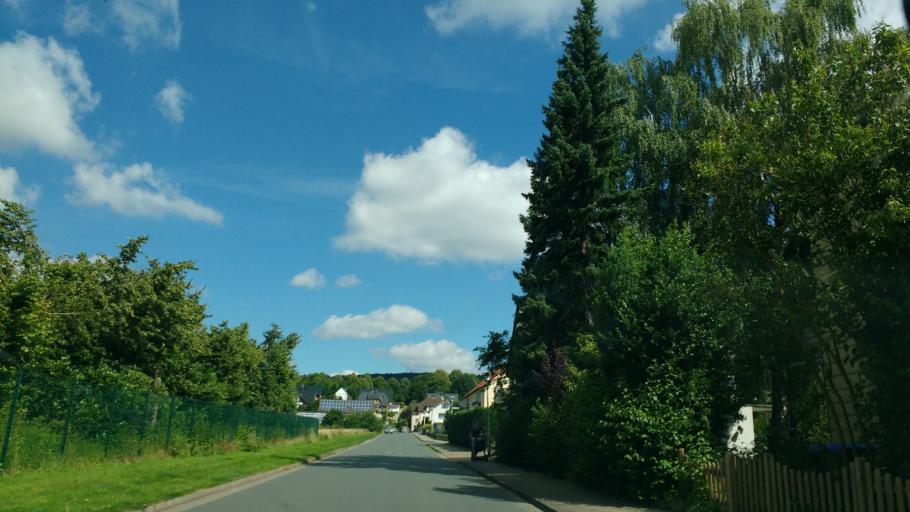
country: DE
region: Lower Saxony
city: Bad Pyrmont
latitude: 51.9849
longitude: 9.2261
